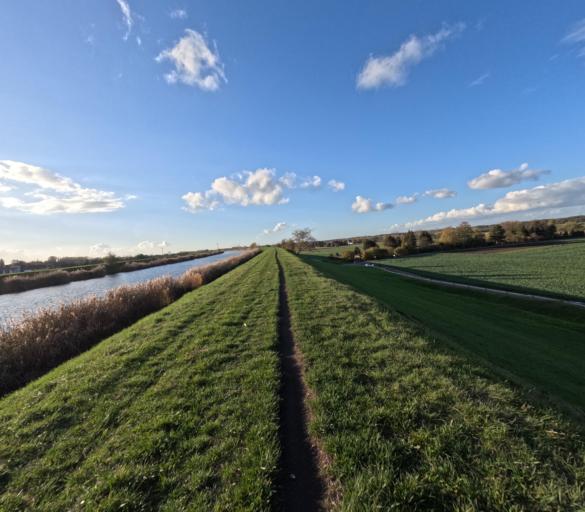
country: DE
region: Saxony
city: Schkeuditz
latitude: 51.3575
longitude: 12.2220
